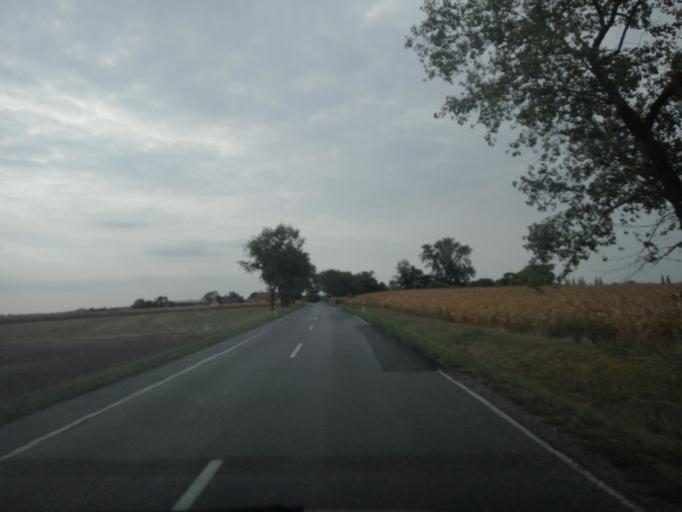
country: PL
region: Lower Silesian Voivodeship
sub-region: Powiat wroclawski
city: Zorawina
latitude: 50.8986
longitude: 17.0629
